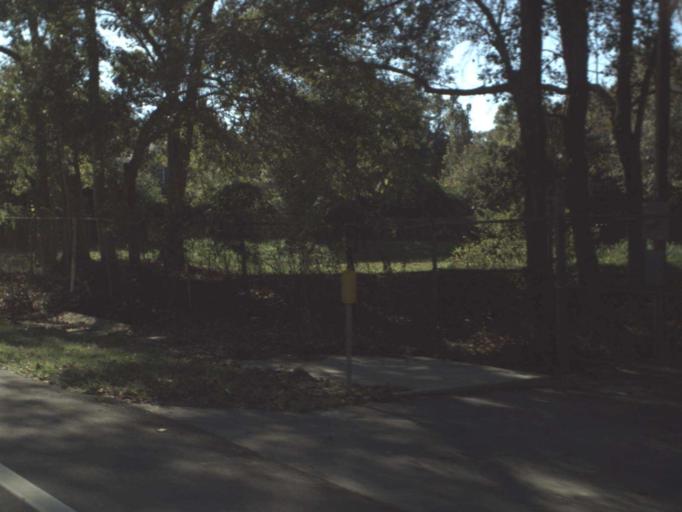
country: US
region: Florida
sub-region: Escambia County
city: Ferry Pass
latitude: 30.5370
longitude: -87.1935
